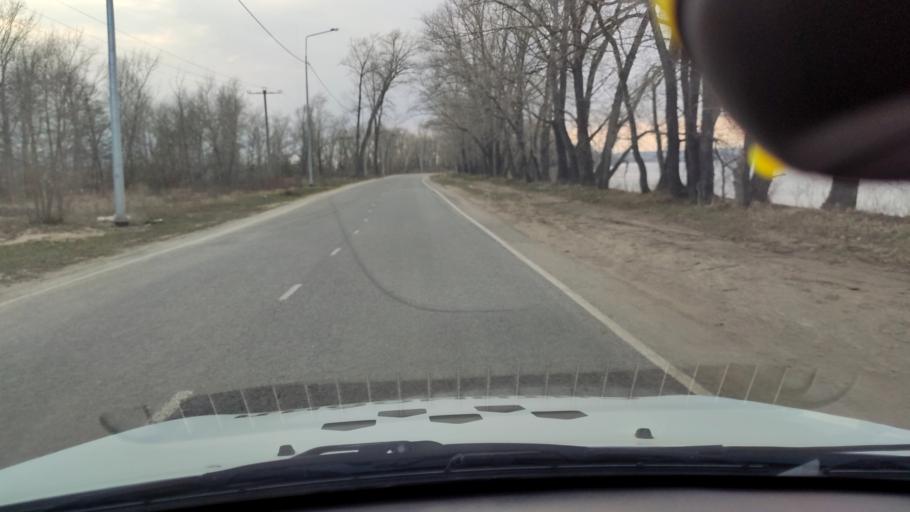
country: RU
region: Samara
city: Zhigulevsk
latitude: 53.4561
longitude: 49.5518
